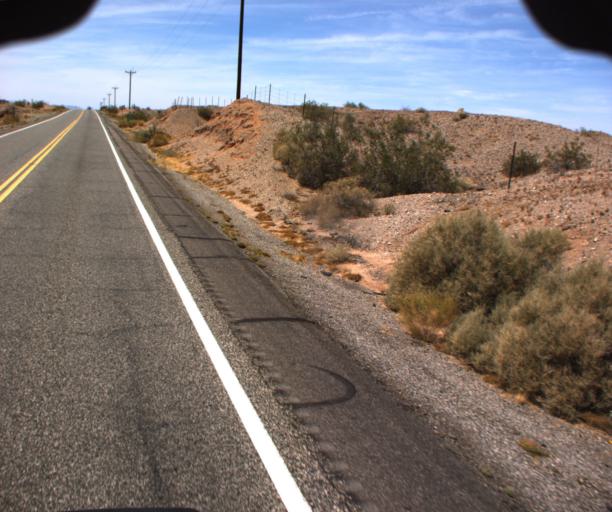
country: US
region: Arizona
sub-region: La Paz County
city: Parker
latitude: 34.0040
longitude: -114.2352
